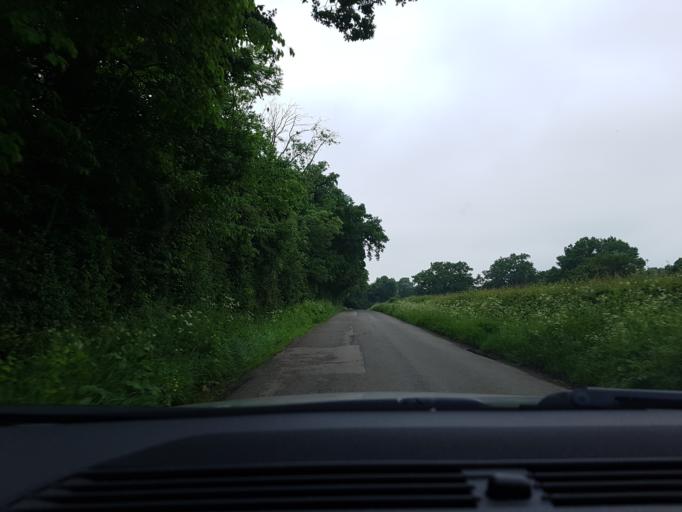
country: GB
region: England
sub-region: Buckinghamshire
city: Steeple Claydon
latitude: 51.9274
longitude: -0.9592
